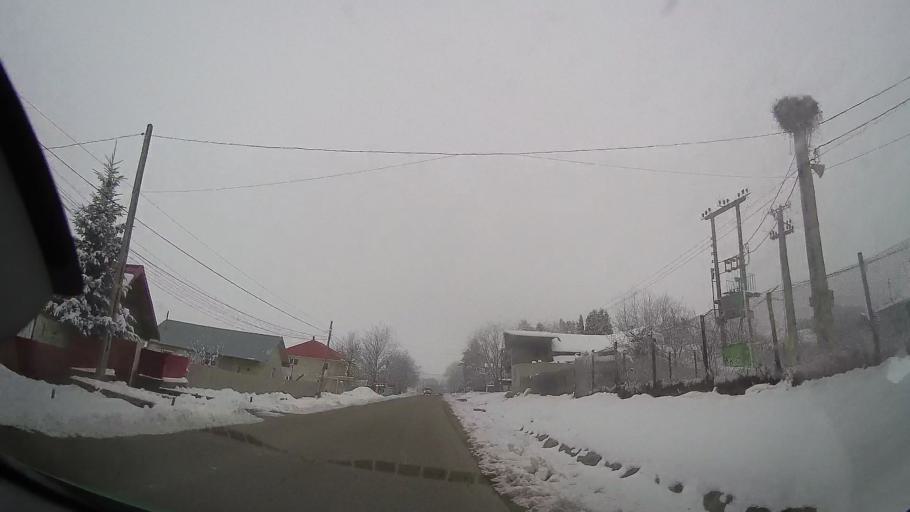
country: RO
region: Neamt
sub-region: Comuna Icusesti
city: Balusesti
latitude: 46.8577
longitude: 27.0246
